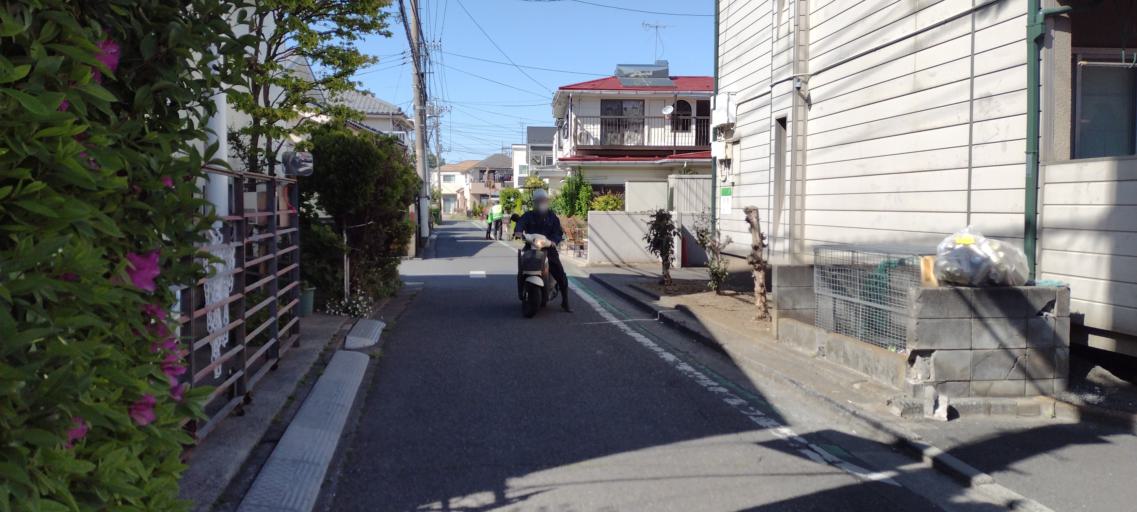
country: JP
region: Tokyo
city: Hino
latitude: 35.6856
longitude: 139.4254
